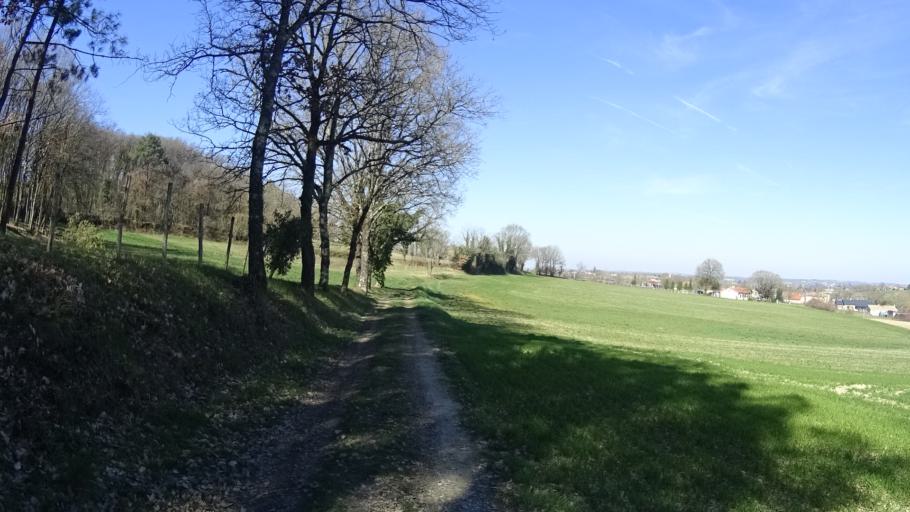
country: FR
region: Aquitaine
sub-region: Departement de la Dordogne
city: Riberac
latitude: 45.2186
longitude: 0.3319
